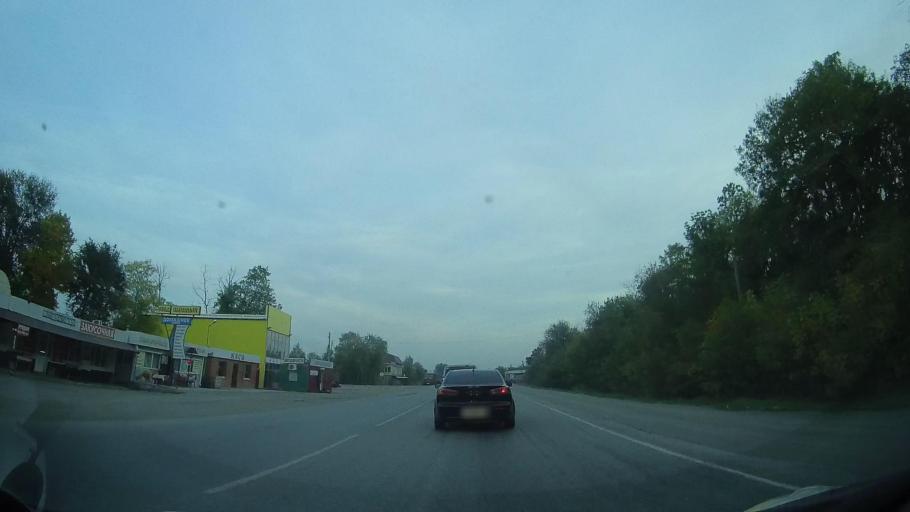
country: RU
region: Rostov
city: Kirovskaya
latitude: 46.9879
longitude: 40.0261
